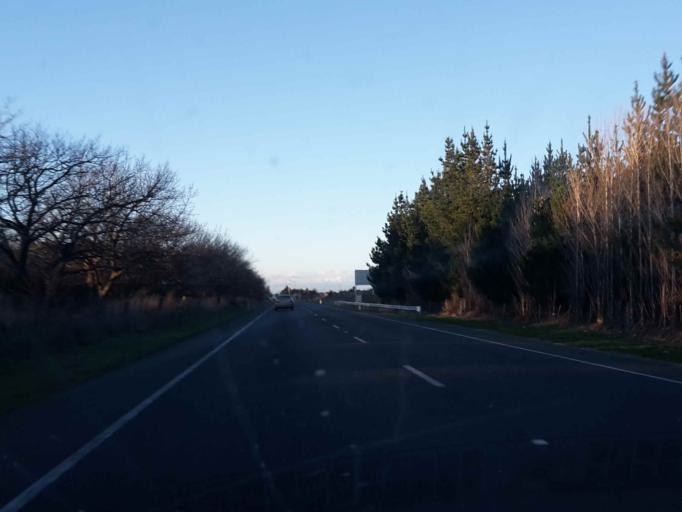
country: NZ
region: Canterbury
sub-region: Selwyn District
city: Rolleston
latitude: -43.5984
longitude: 172.3590
